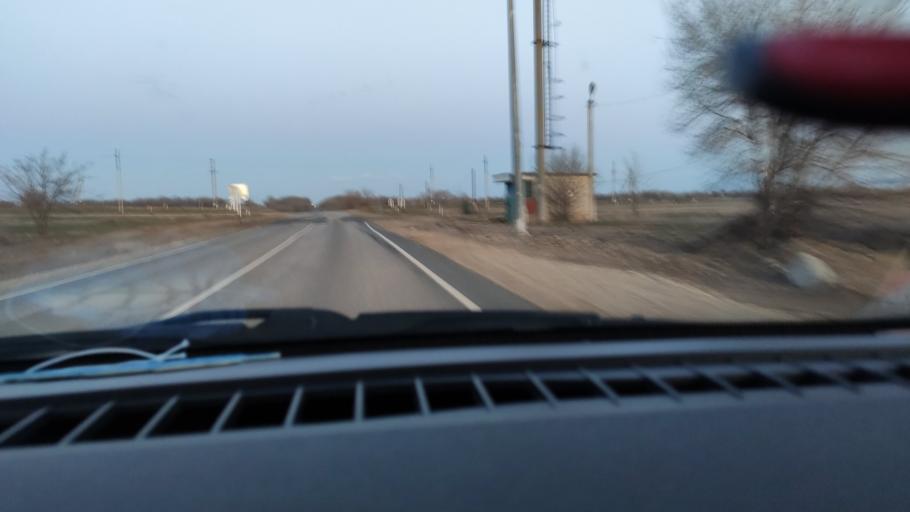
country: RU
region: Saratov
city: Krasnoarmeysk
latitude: 51.0818
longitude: 45.9635
